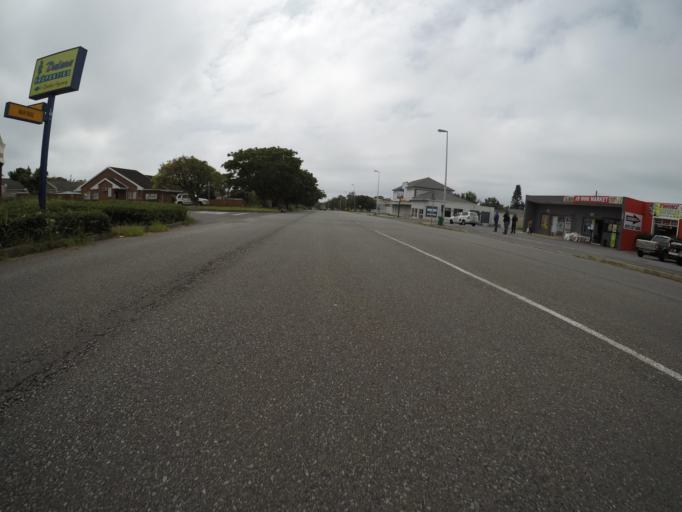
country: ZA
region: Eastern Cape
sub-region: Buffalo City Metropolitan Municipality
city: East London
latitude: -32.9386
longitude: 28.0119
